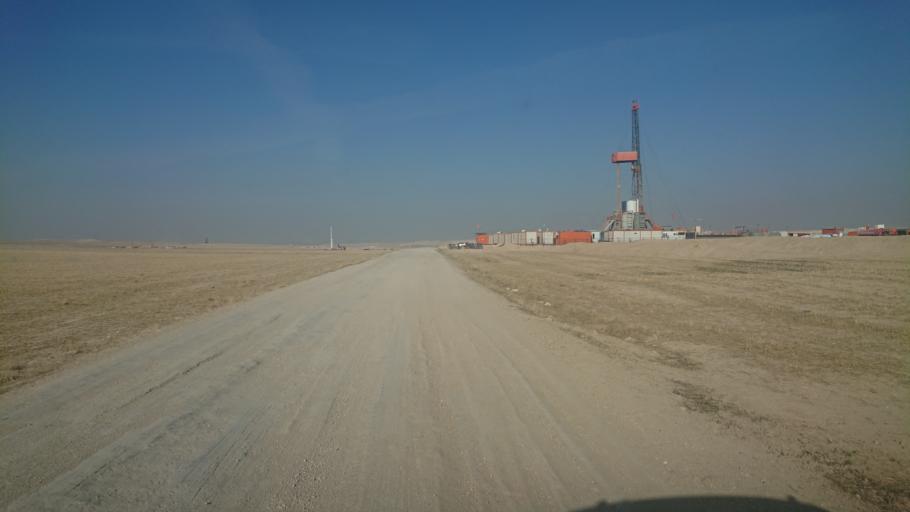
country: TR
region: Aksaray
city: Sultanhani
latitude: 38.0571
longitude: 33.6137
